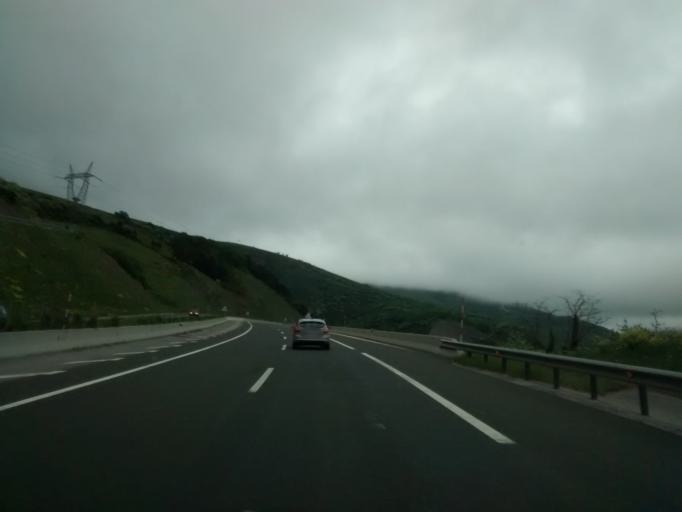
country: ES
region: Cantabria
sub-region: Provincia de Cantabria
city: Reinosa
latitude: 43.0252
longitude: -4.1134
